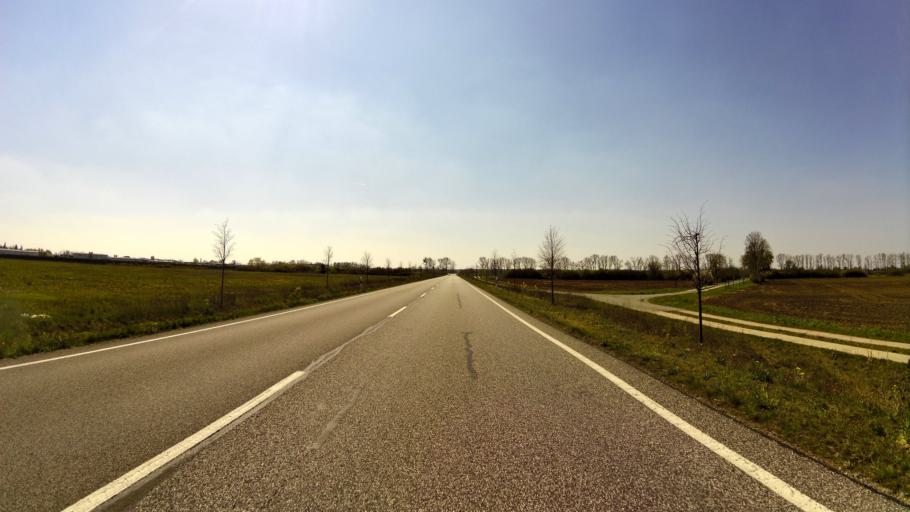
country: DE
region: Saxony-Anhalt
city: Oebisfelde
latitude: 52.4427
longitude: 10.9715
